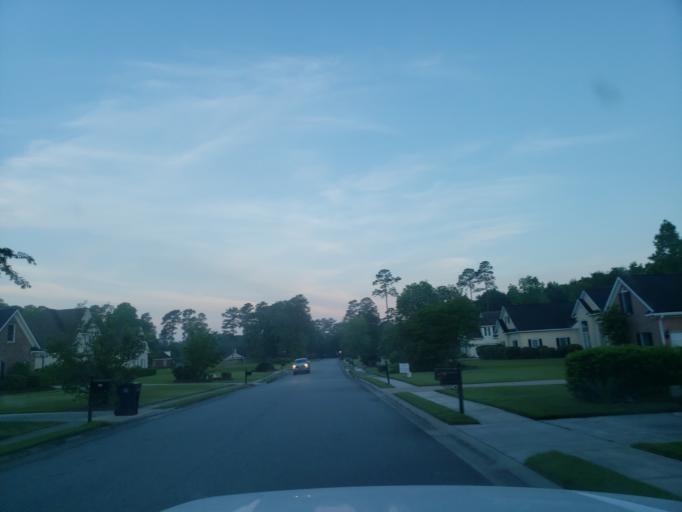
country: US
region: Georgia
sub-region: Chatham County
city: Pooler
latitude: 32.0713
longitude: -81.2305
